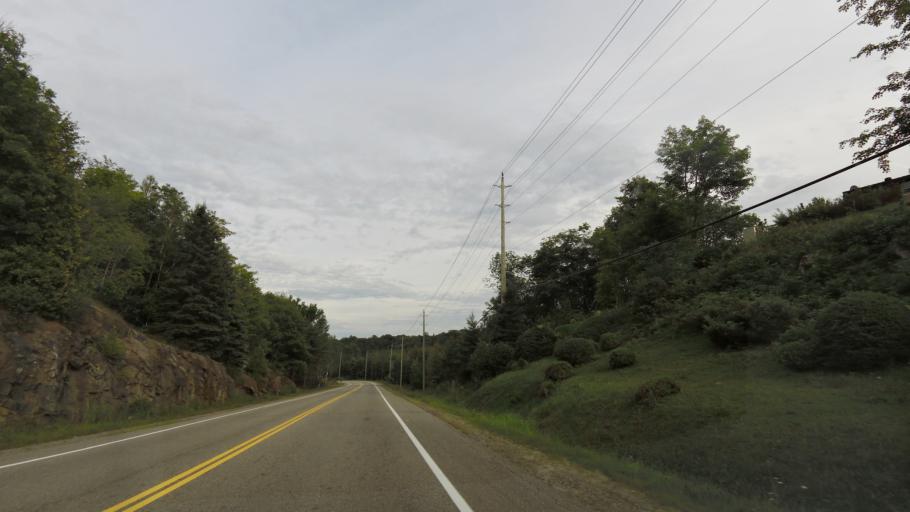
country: CA
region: Ontario
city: Bancroft
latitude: 45.0398
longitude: -78.4764
